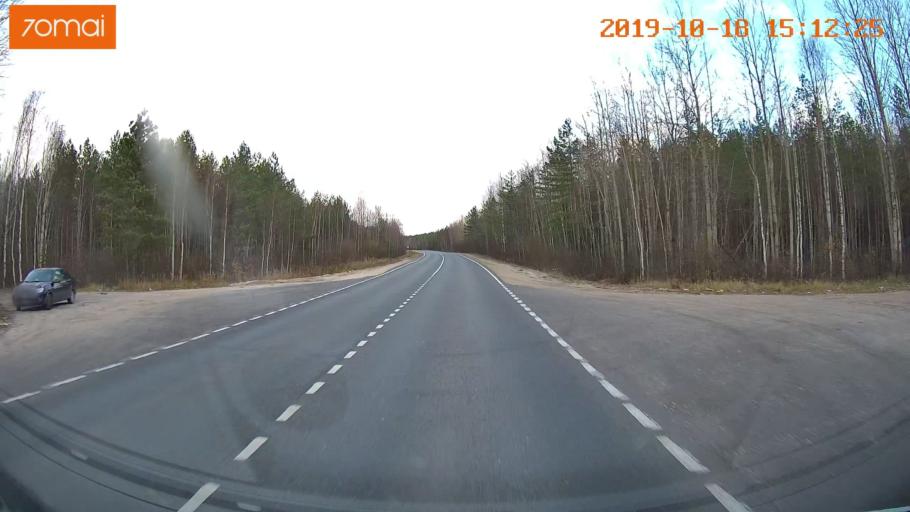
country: RU
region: Vladimir
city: Gus'-Khrustal'nyy
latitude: 55.5760
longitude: 40.6973
